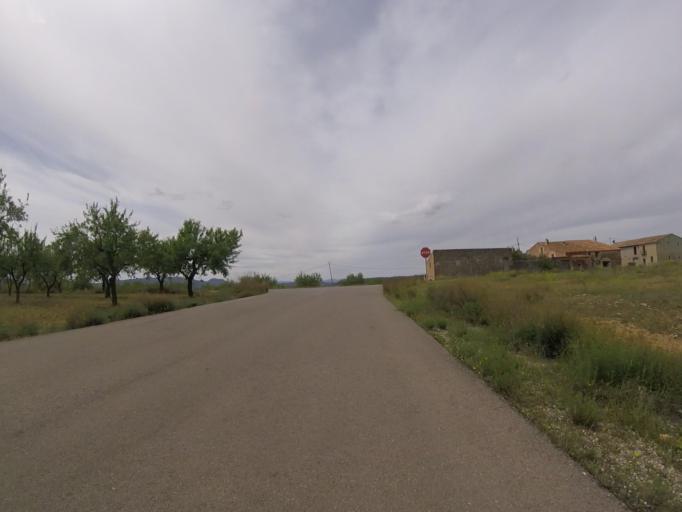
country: ES
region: Valencia
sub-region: Provincia de Castello
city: Benlloch
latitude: 40.1994
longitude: -0.0085
